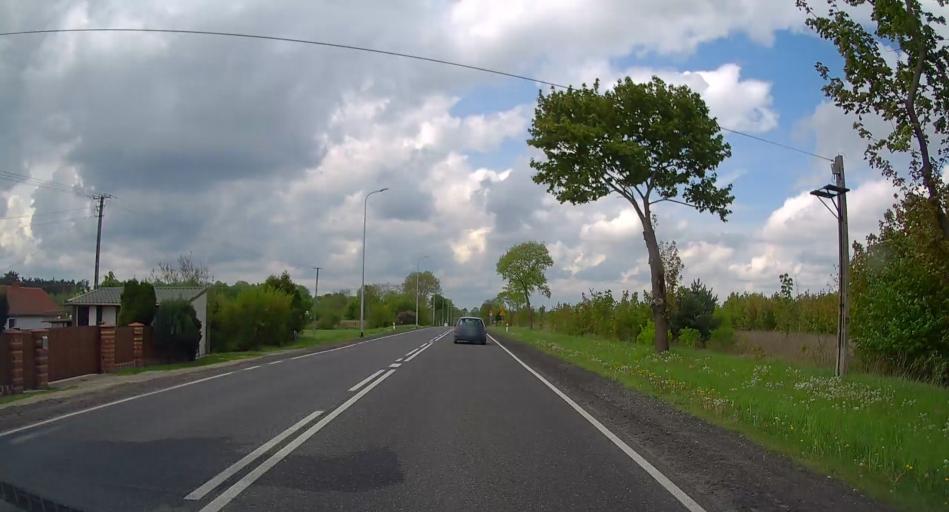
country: PL
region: Masovian Voivodeship
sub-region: Powiat nowodworski
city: Zakroczym
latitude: 52.4412
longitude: 20.5505
